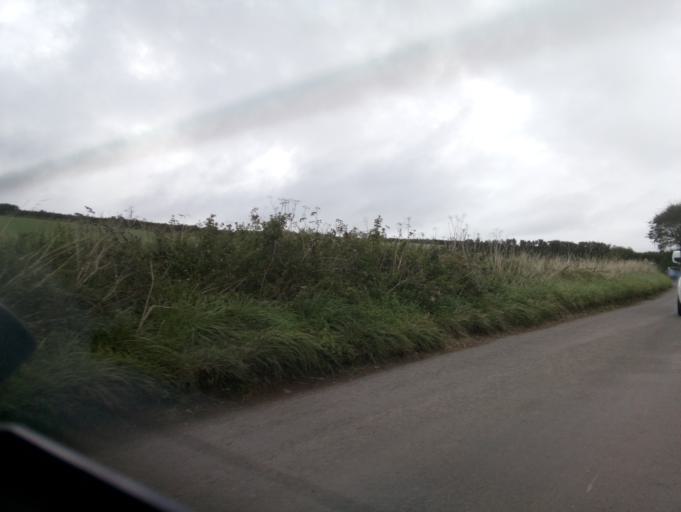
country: GB
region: England
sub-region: Devon
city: Kingsbridge
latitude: 50.2686
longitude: -3.8177
